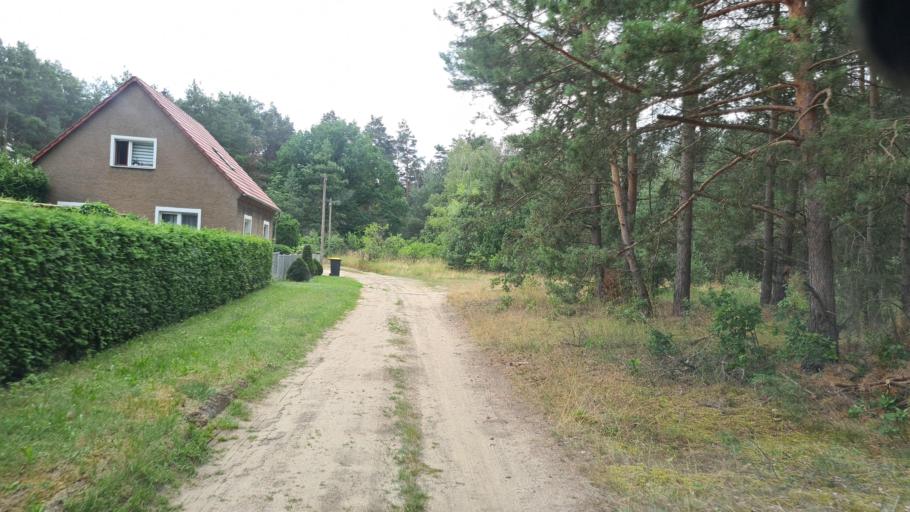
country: DE
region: Brandenburg
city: Finsterwalde
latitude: 51.6572
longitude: 13.7759
